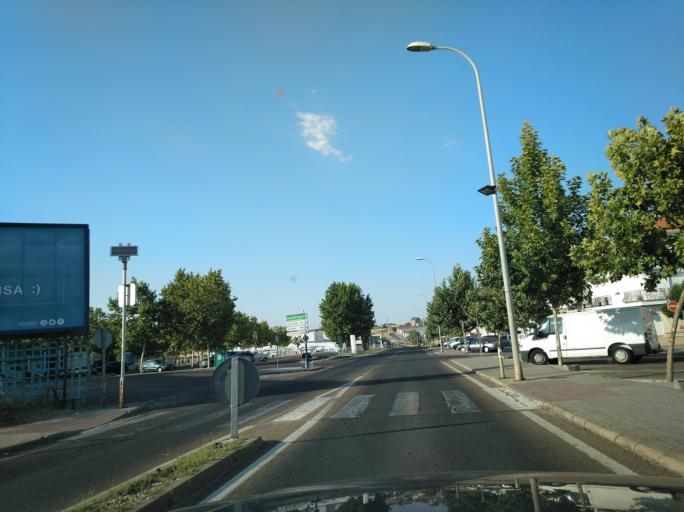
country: ES
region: Extremadura
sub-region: Provincia de Badajoz
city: Olivenza
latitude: 38.6902
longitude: -7.0933
